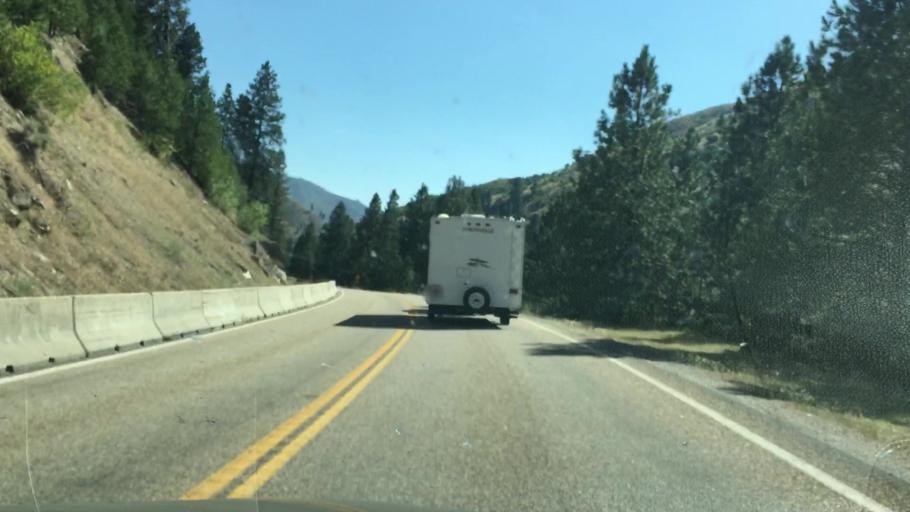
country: US
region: Idaho
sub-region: Boise County
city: Idaho City
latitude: 44.0809
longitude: -116.1213
